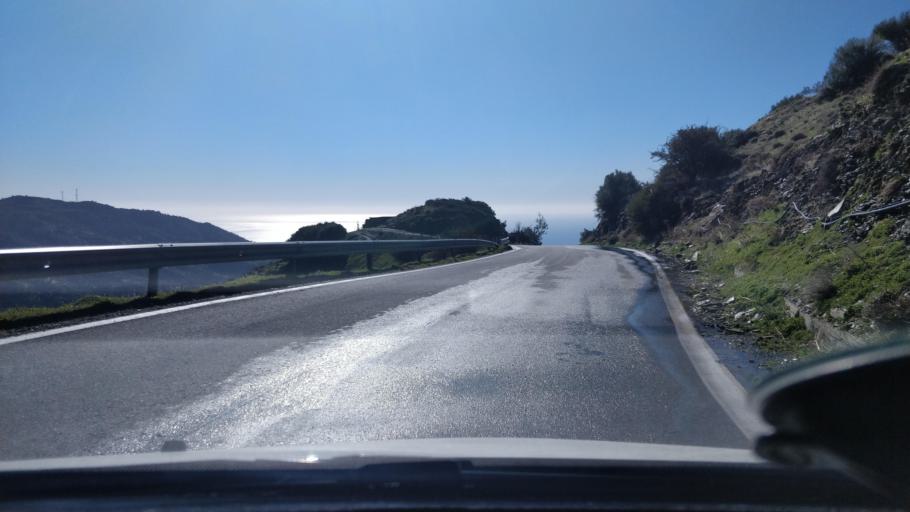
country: GR
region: Crete
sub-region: Nomos Irakleiou
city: Kastelli
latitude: 35.0381
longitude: 25.4454
